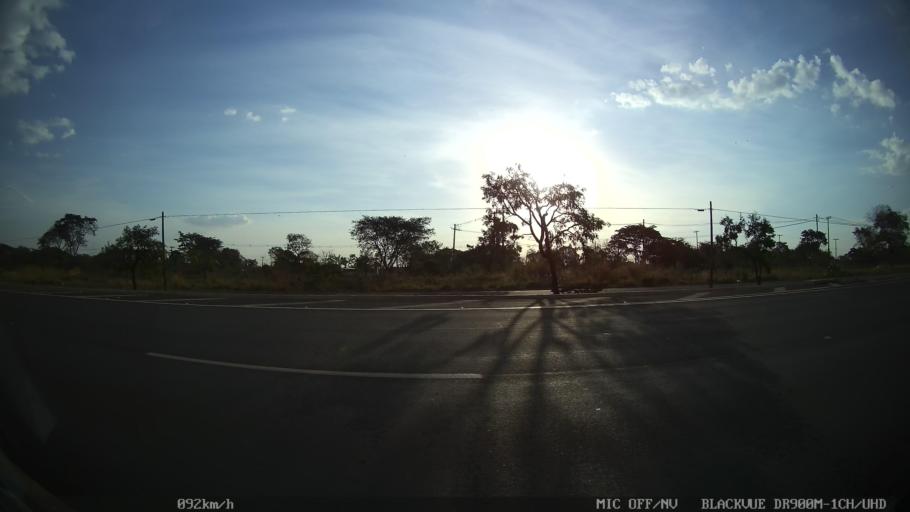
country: BR
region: Sao Paulo
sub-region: Ribeirao Preto
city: Ribeirao Preto
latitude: -21.1187
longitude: -47.7858
